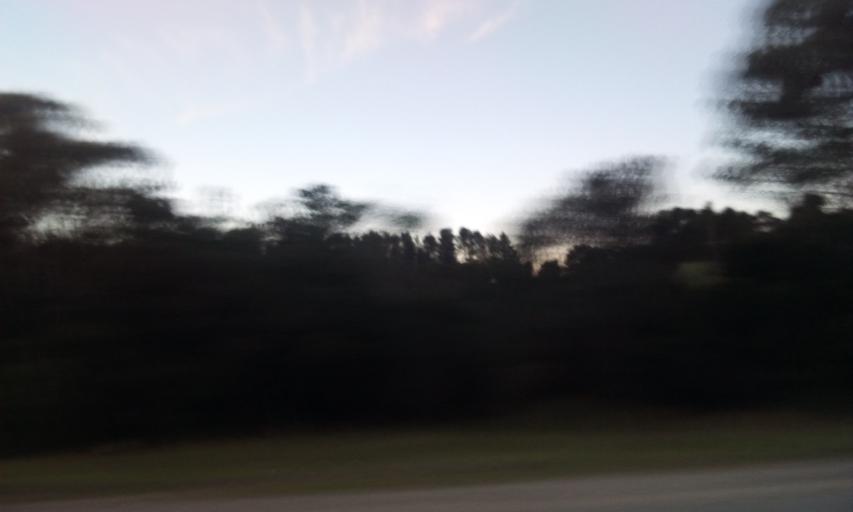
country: AU
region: New South Wales
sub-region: Wingecarribee
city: Bundanoon
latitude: -34.6923
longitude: 150.0333
